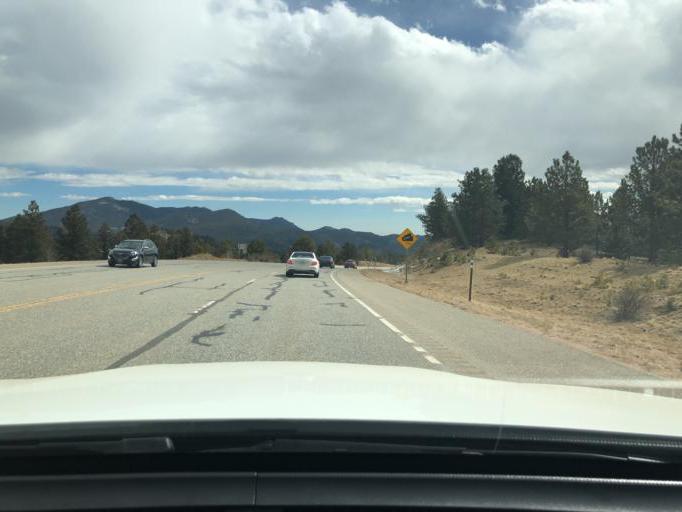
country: US
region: Colorado
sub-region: Gilpin County
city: Central City
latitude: 39.7891
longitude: -105.5009
